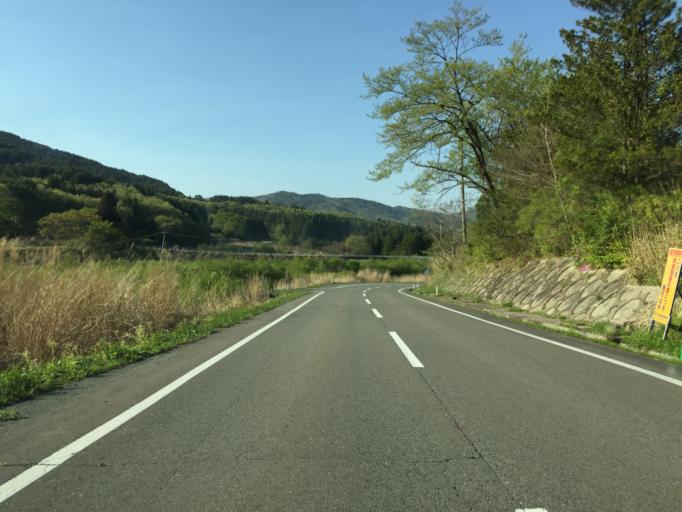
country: JP
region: Fukushima
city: Funehikimachi-funehiki
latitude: 37.5512
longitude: 140.7363
